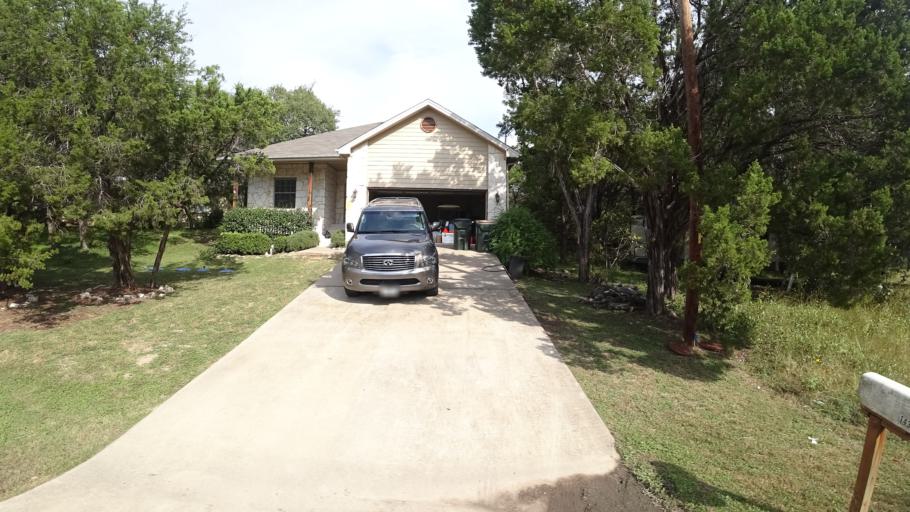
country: US
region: Texas
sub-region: Travis County
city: Hudson Bend
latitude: 30.3819
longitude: -97.9195
